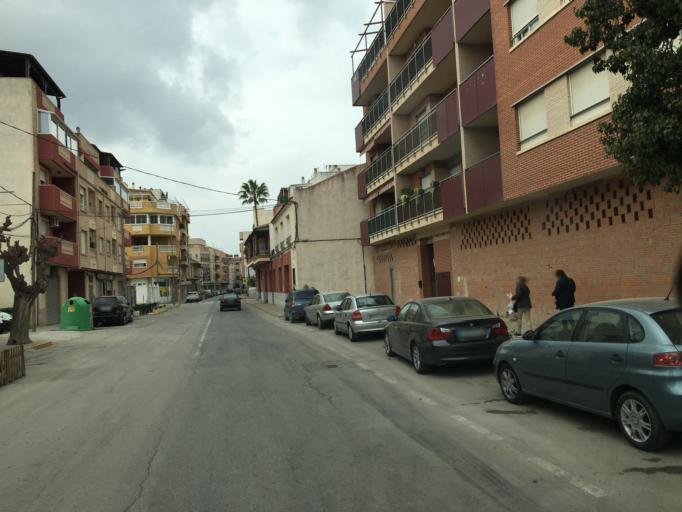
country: ES
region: Murcia
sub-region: Murcia
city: Beniel
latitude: 38.0476
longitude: -0.9991
